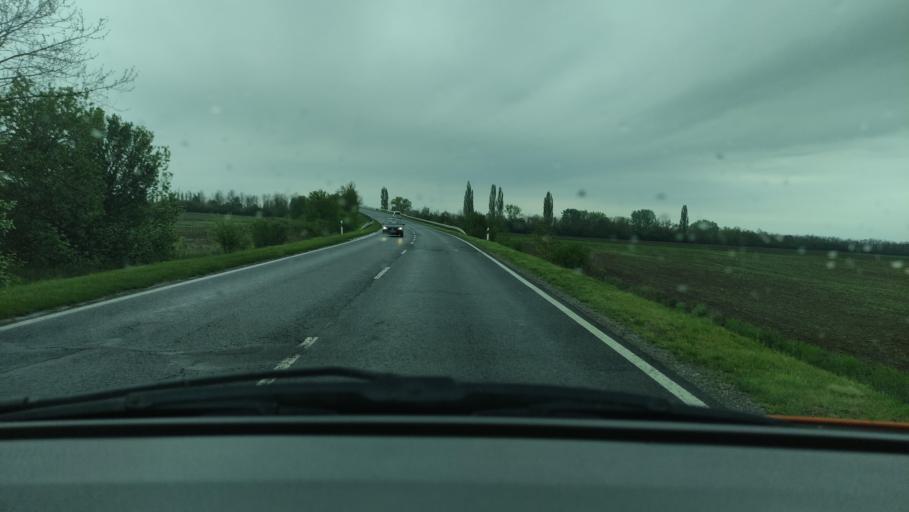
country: HU
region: Baranya
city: Mohacs
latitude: 45.9937
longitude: 18.6548
